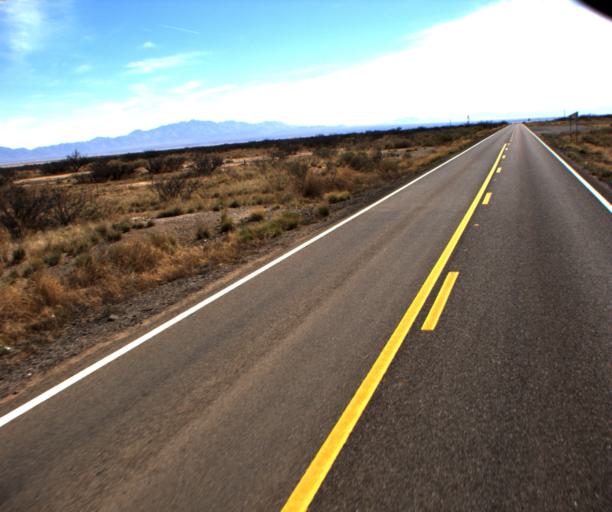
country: US
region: Arizona
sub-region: Cochise County
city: Willcox
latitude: 32.1401
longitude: -109.9240
